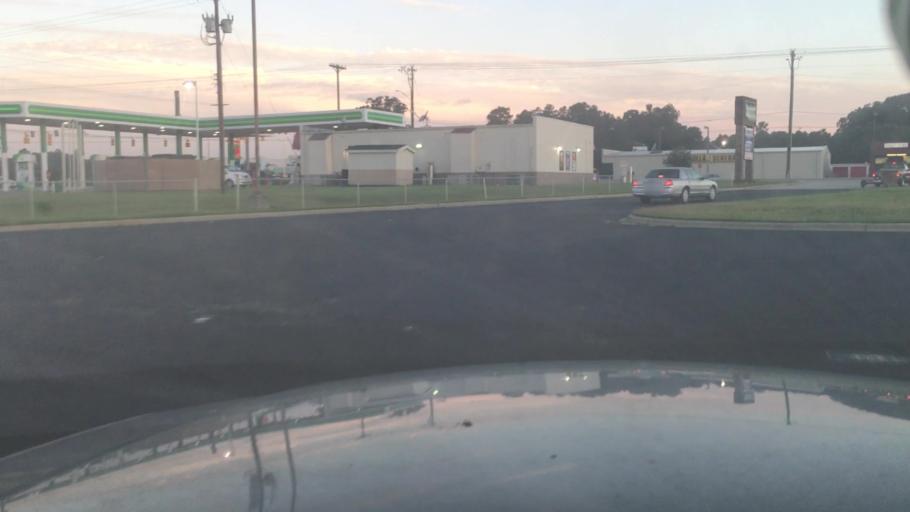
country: US
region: North Carolina
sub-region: Hoke County
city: Rockfish
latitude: 35.0587
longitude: -79.0477
